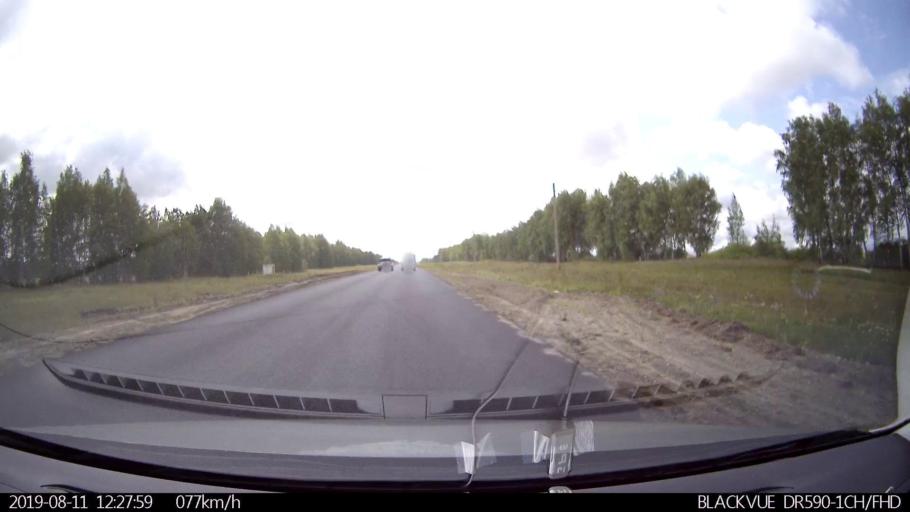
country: RU
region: Ulyanovsk
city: Ignatovka
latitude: 53.8483
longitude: 47.9156
